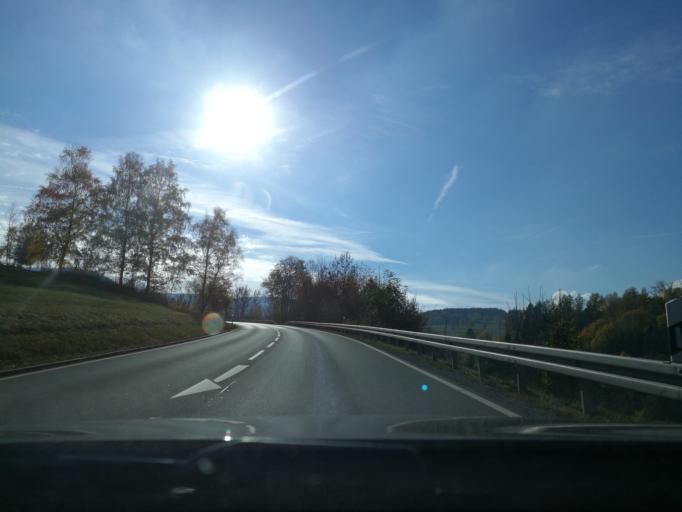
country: DE
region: Hesse
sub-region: Regierungsbezirk Kassel
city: Gersfeld
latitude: 50.4419
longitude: 9.9168
